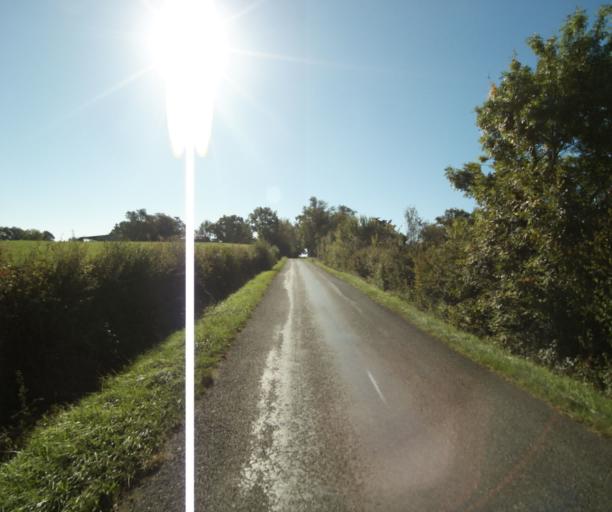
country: FR
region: Midi-Pyrenees
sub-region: Departement du Gers
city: Gondrin
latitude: 43.8106
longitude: 0.2267
